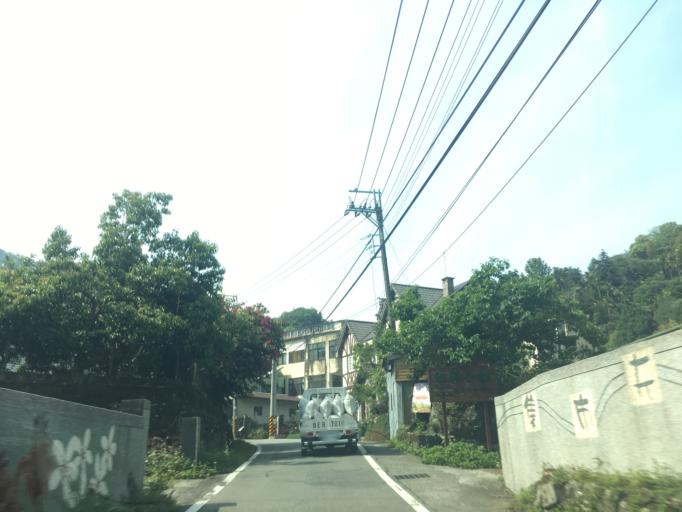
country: TW
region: Taiwan
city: Fengyuan
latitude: 24.1596
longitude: 120.8265
